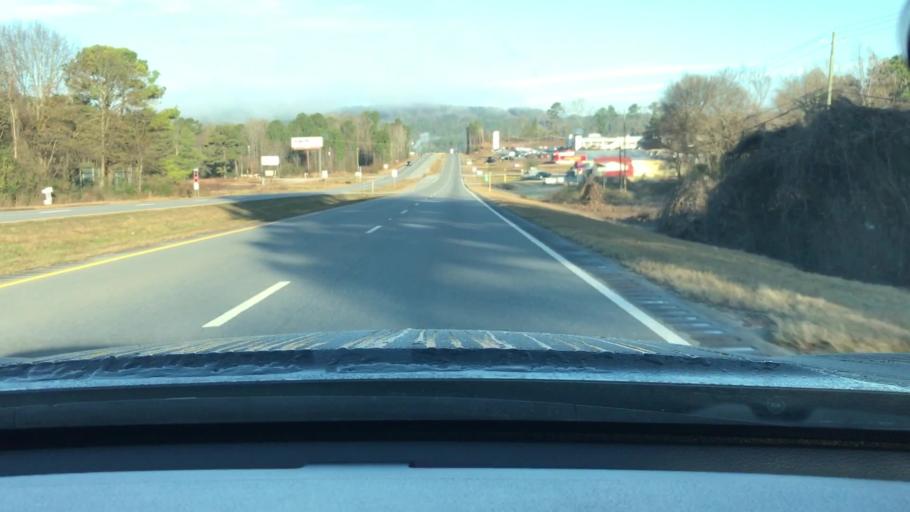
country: US
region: Alabama
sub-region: Talladega County
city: Mignon
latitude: 33.1847
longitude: -86.3019
